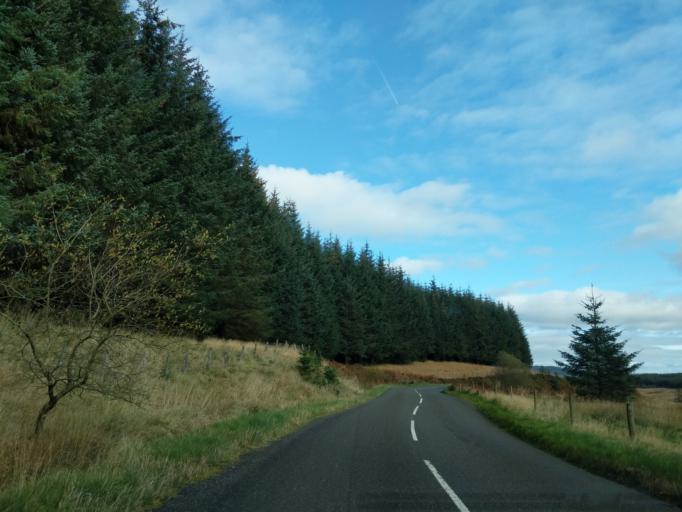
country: GB
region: Scotland
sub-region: Dumfries and Galloway
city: Castle Douglas
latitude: 55.1398
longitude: -4.0448
